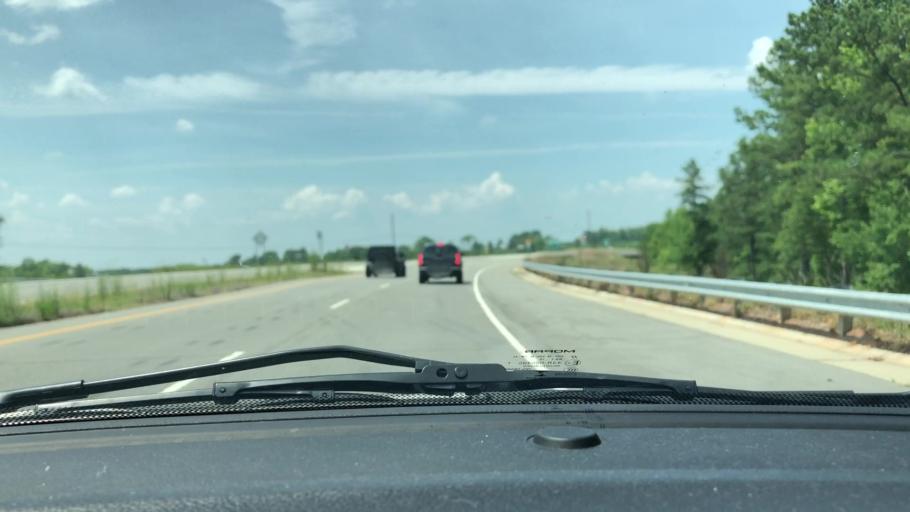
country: US
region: North Carolina
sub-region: Chatham County
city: Farmville
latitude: 35.5380
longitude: -79.2397
